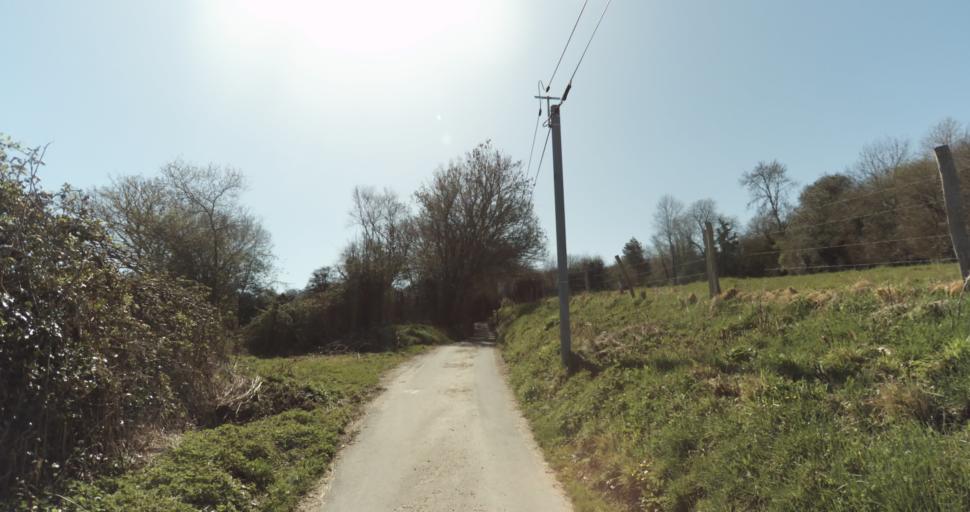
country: FR
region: Lower Normandy
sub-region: Departement du Calvados
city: Saint-Pierre-sur-Dives
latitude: 49.0131
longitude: 0.0439
